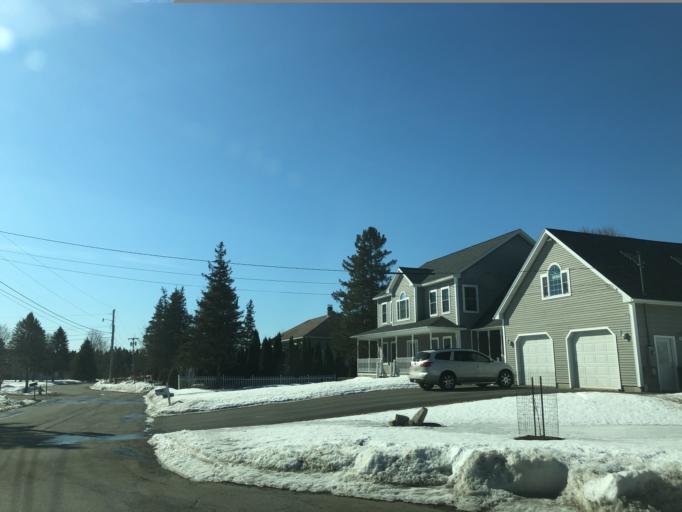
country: US
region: Maine
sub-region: Penobscot County
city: Brewer
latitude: 44.8193
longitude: -68.7526
